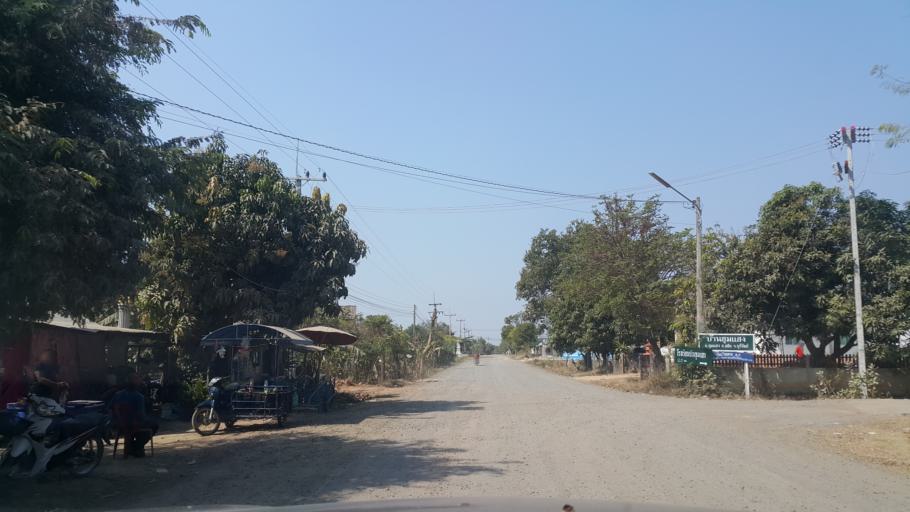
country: TH
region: Buriram
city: Satuek
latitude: 15.1325
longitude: 103.3497
